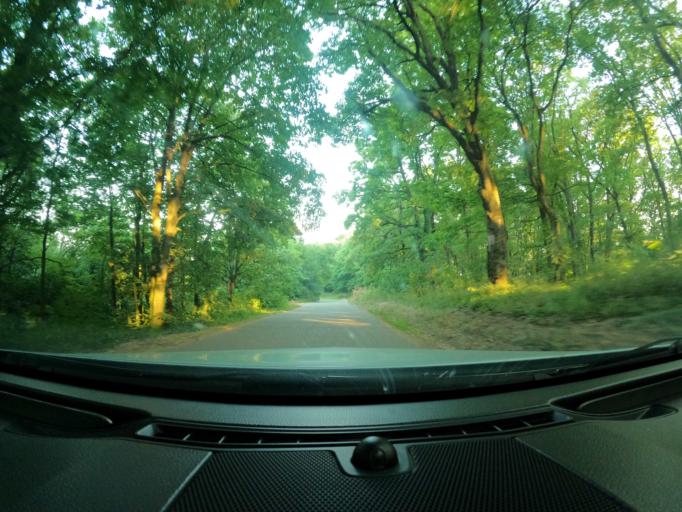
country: RS
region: Autonomna Pokrajina Vojvodina
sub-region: Juznobacki Okrug
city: Beocin
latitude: 45.1574
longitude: 19.7423
